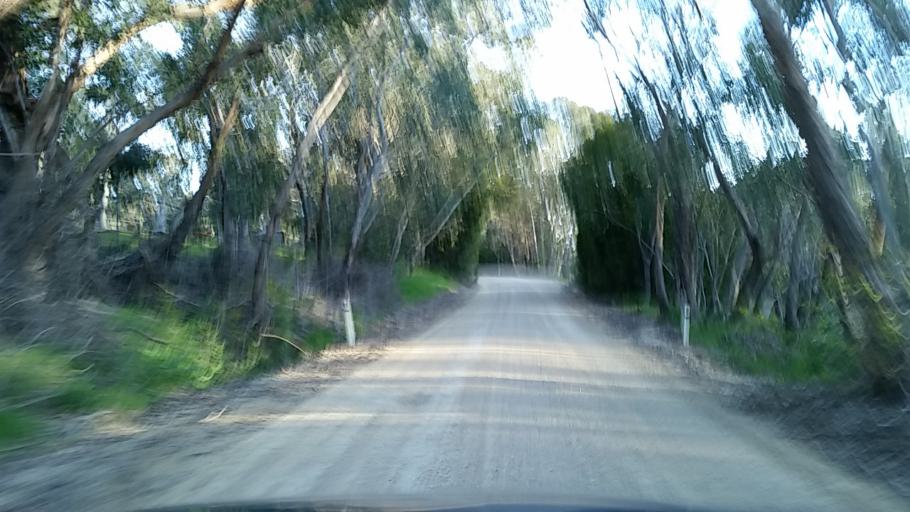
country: AU
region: South Australia
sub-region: Mount Barker
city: Meadows
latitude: -35.2712
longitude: 138.7016
